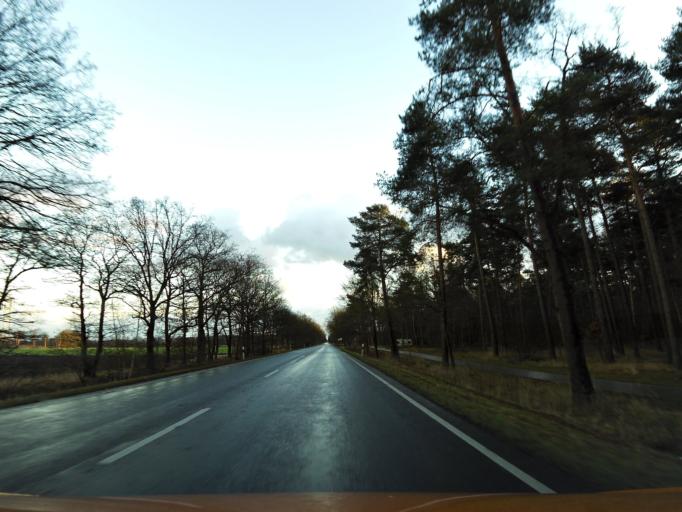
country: DE
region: Lower Saxony
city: Uetze
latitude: 52.4722
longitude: 10.2765
